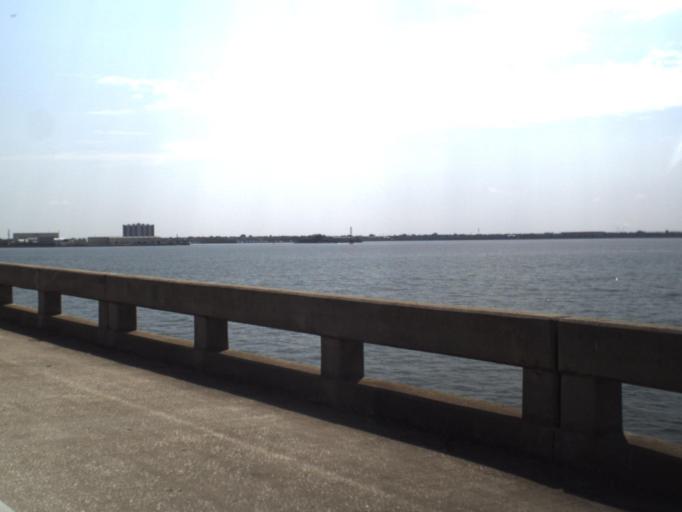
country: US
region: Florida
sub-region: Pinellas County
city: Gandy
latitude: 27.8864
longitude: -82.5565
